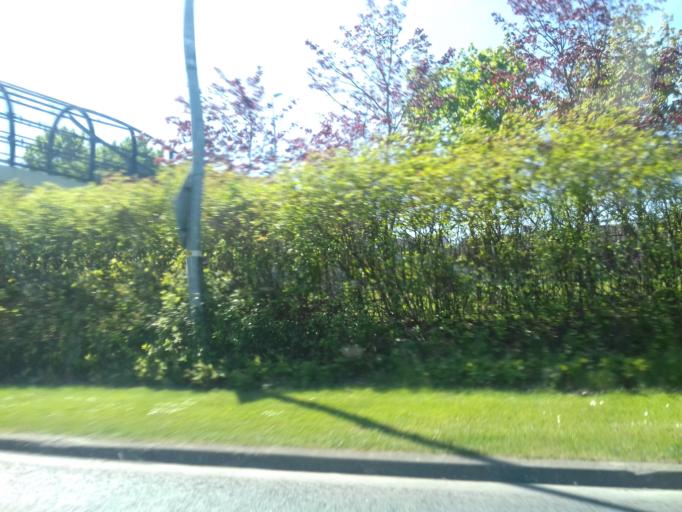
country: IE
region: Leinster
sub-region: Dublin City
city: Finglas
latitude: 53.3959
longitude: -6.3053
